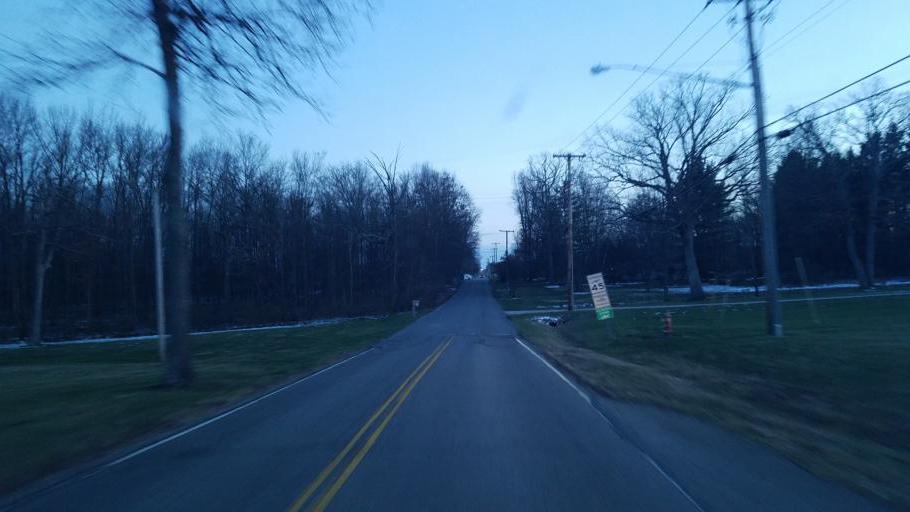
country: US
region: Ohio
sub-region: Ashland County
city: Ashland
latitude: 40.8530
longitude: -82.2793
